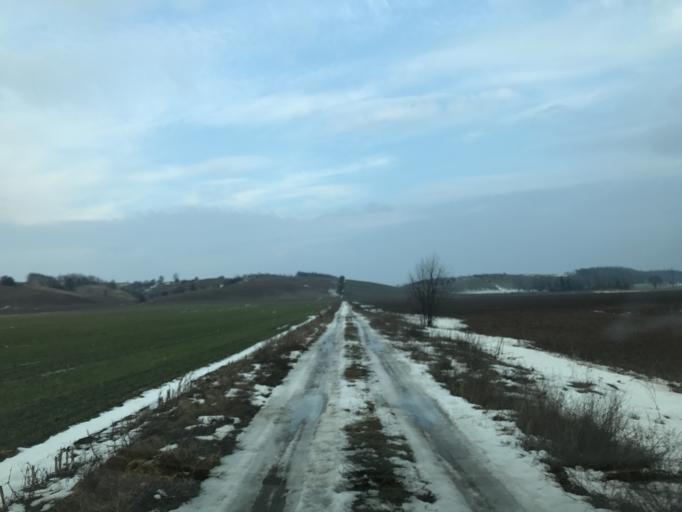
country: PL
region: Kujawsko-Pomorskie
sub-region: Powiat brodnicki
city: Brzozie
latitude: 53.2992
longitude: 19.5619
